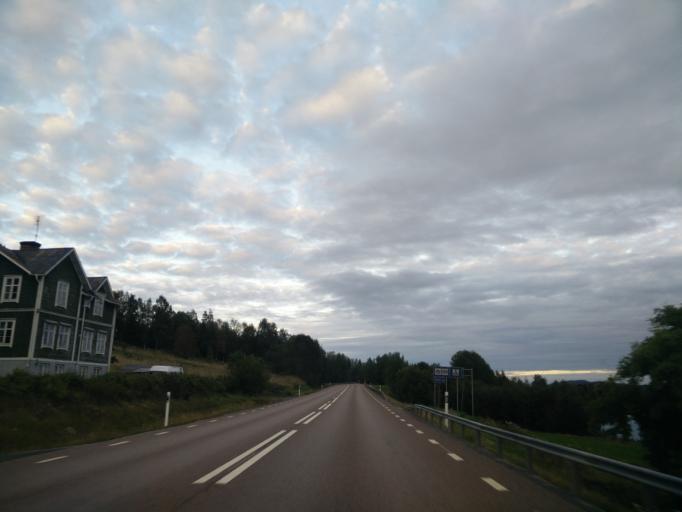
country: SE
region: Vaesternorrland
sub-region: Kramfors Kommun
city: Nordingra
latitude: 62.9201
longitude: 18.0569
